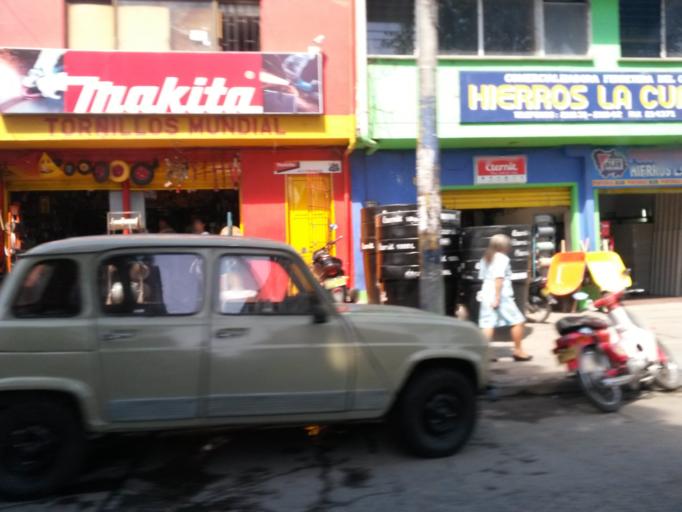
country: CO
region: Cauca
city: Popayan
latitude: 2.4455
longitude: -76.6153
